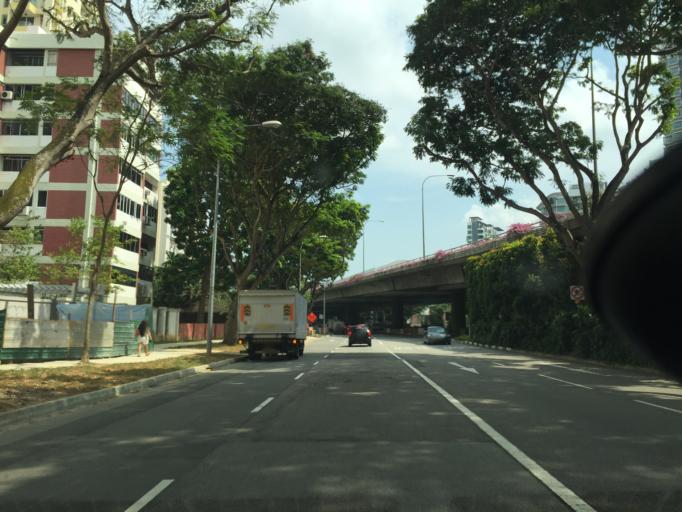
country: SG
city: Singapore
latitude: 1.3152
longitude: 103.8465
